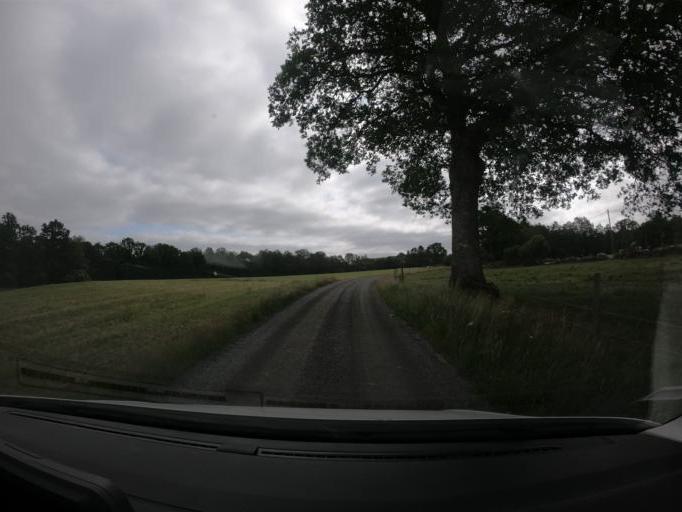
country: SE
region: Skane
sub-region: Eslovs Kommun
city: Stehag
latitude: 55.9681
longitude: 13.3591
